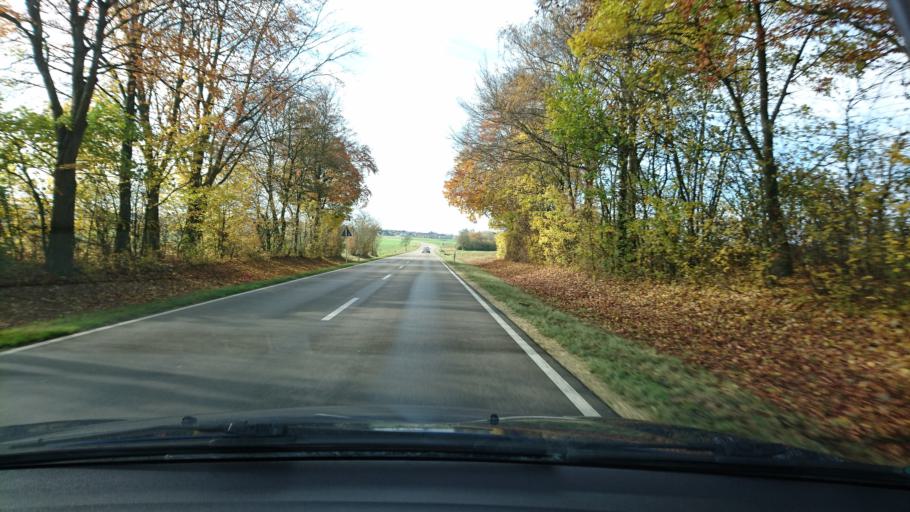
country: DE
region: Bavaria
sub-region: Swabia
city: Bissingen
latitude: 48.7231
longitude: 10.5759
